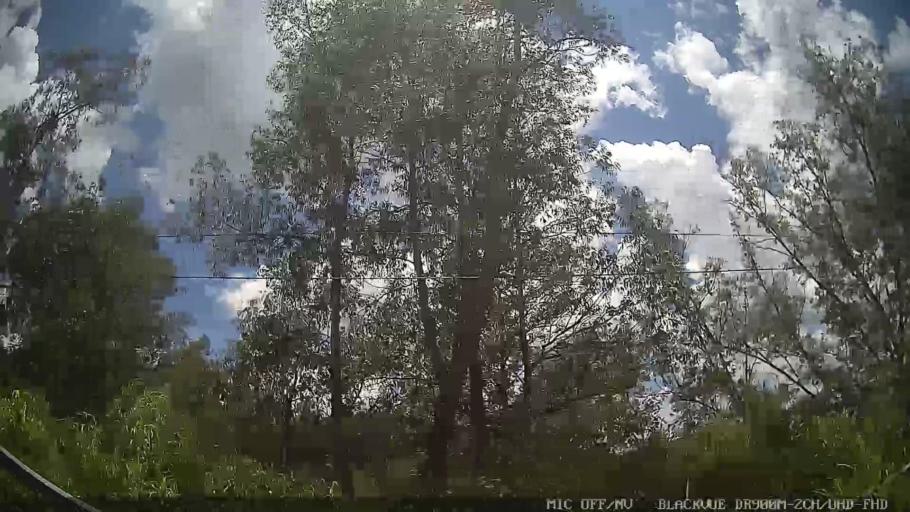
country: BR
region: Sao Paulo
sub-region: Amparo
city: Amparo
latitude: -22.6557
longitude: -46.7443
